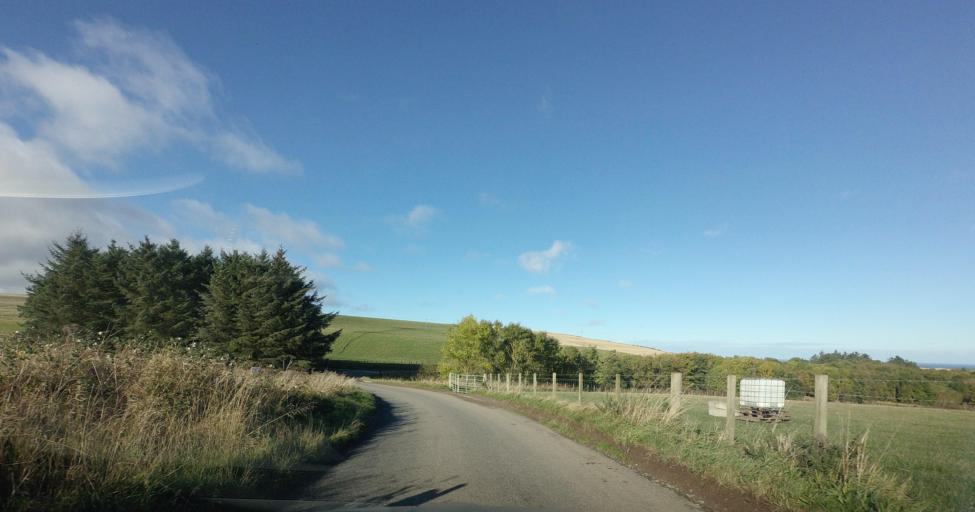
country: GB
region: Scotland
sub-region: Aberdeenshire
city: Macduff
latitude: 57.6635
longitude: -2.3217
